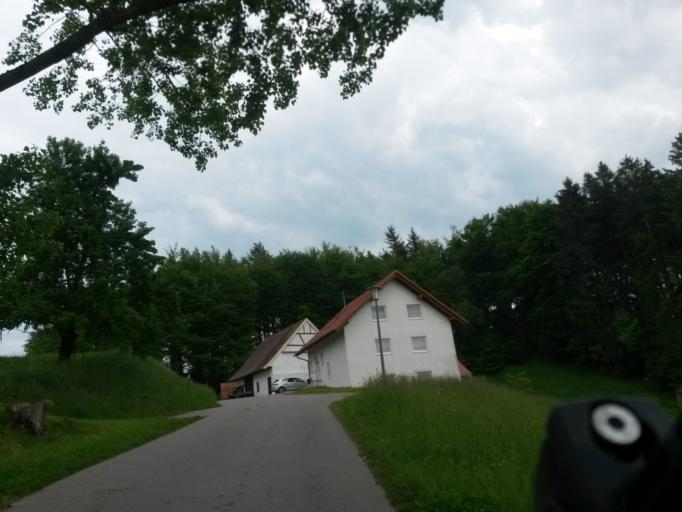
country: DE
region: Baden-Wuerttemberg
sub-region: Tuebingen Region
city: Wolfegg
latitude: 47.8521
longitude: 9.7979
